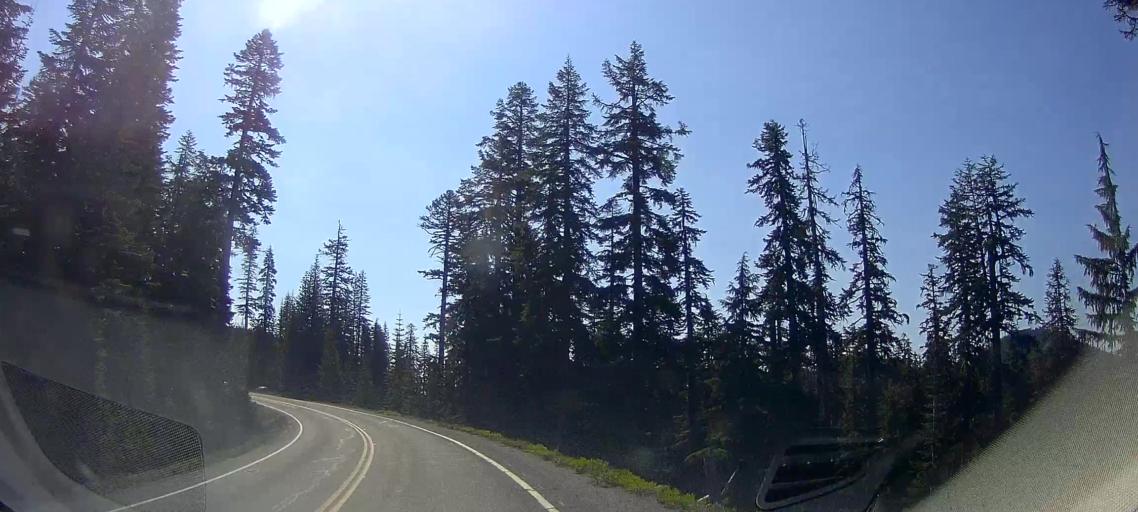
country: US
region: Oregon
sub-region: Klamath County
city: Klamath Falls
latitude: 42.8764
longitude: -122.1062
